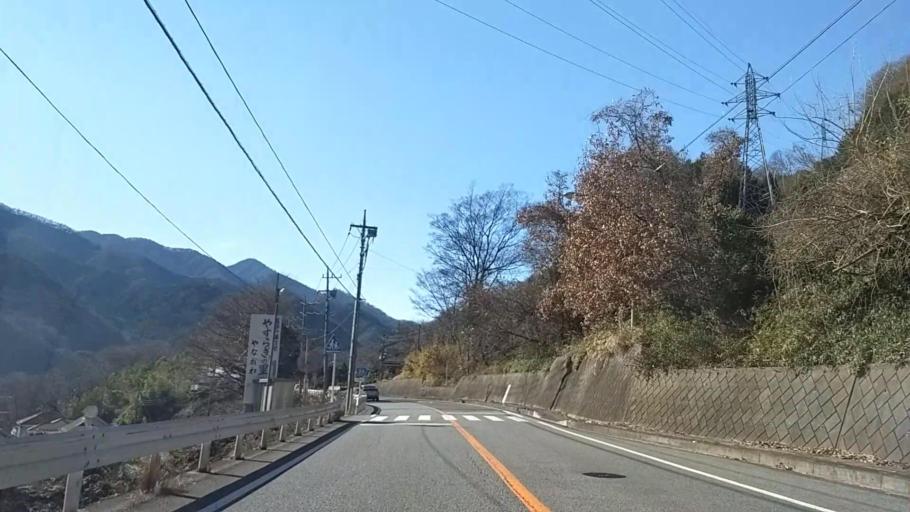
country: JP
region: Yamanashi
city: Uenohara
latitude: 35.6056
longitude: 139.0284
